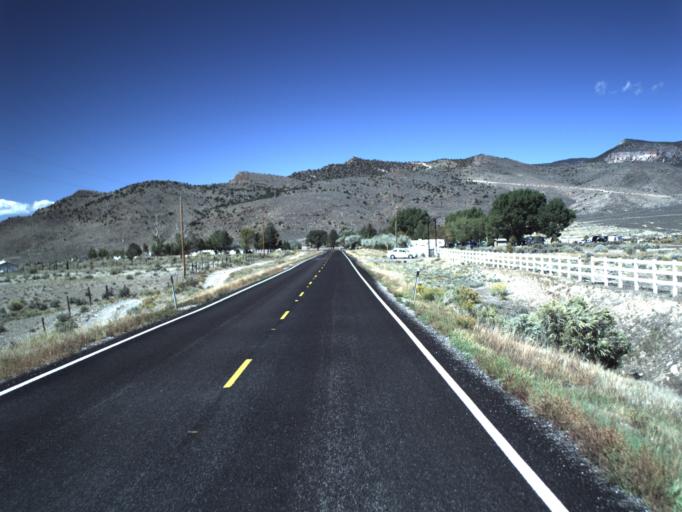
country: US
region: Utah
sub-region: Piute County
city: Junction
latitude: 38.1636
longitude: -112.0134
